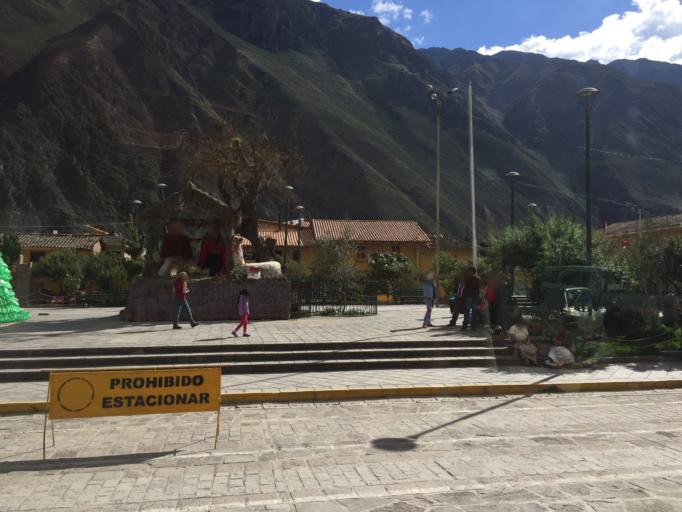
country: PE
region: Cusco
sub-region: Provincia de Urubamba
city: Ollantaytambo
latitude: -13.2584
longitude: -72.2634
